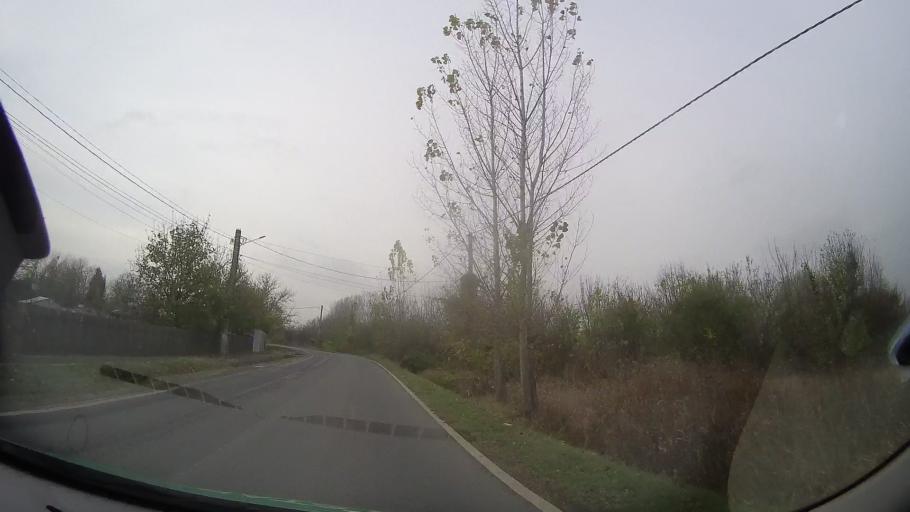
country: RO
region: Ilfov
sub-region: Comuna Gruiu
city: Silistea Snagovului
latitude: 44.7503
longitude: 26.1947
